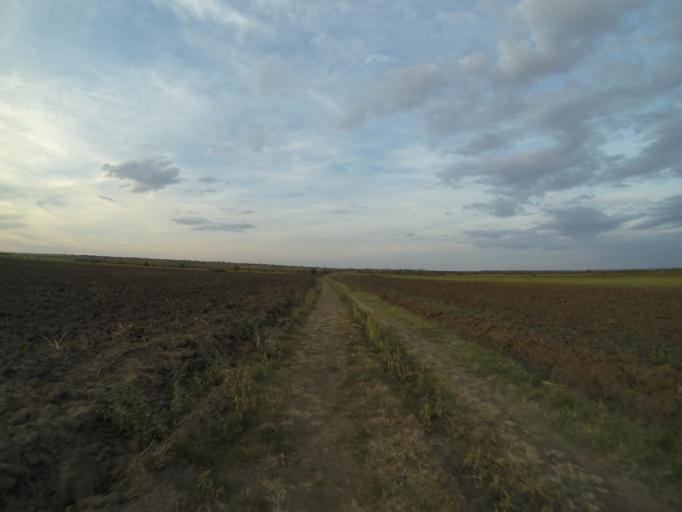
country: RO
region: Dolj
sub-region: Comuna Ceratu
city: Ceratu
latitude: 44.0946
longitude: 23.6753
